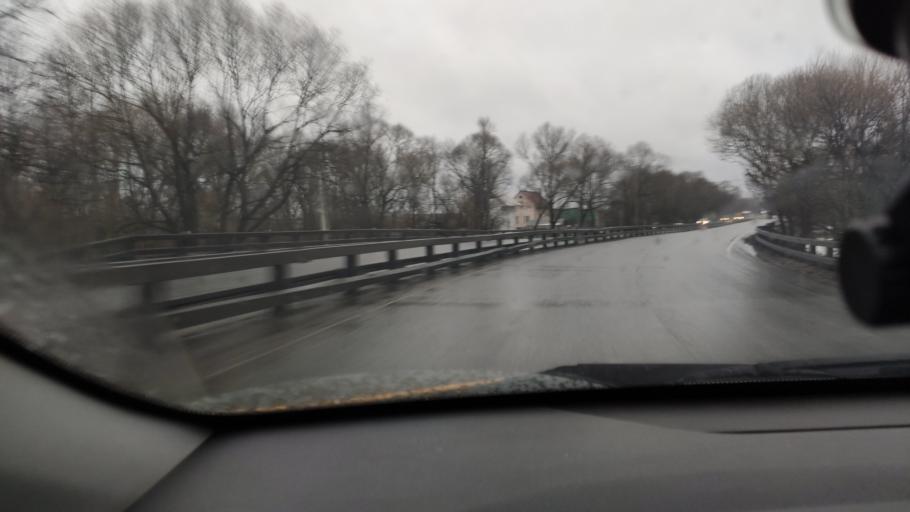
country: RU
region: Moskovskaya
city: Troitsk
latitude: 55.3036
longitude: 37.2177
